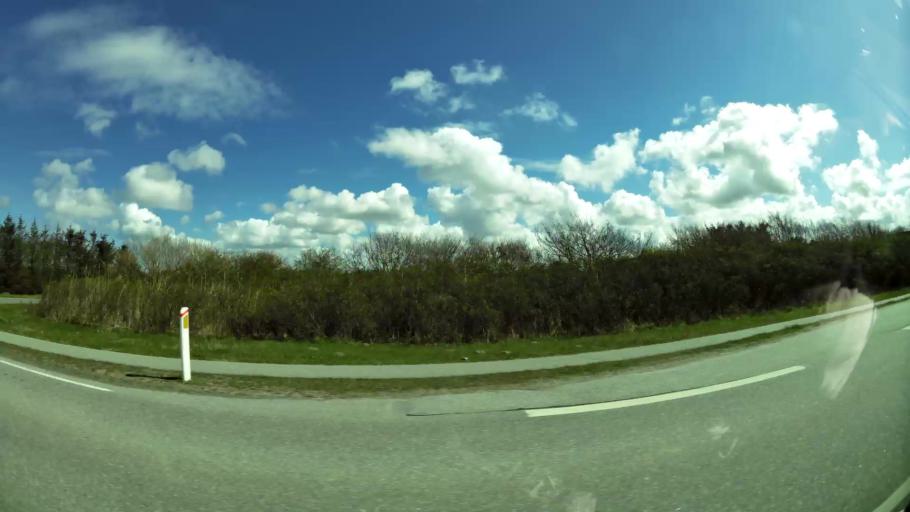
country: DK
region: North Denmark
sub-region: Hjorring Kommune
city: Hirtshals
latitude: 57.5558
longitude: 9.9389
